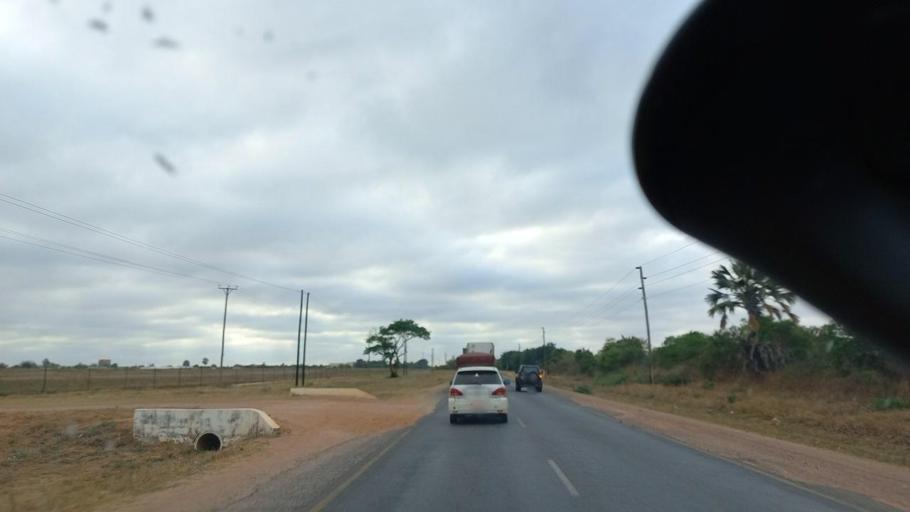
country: ZM
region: Lusaka
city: Chongwe
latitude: -15.3447
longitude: 28.5252
